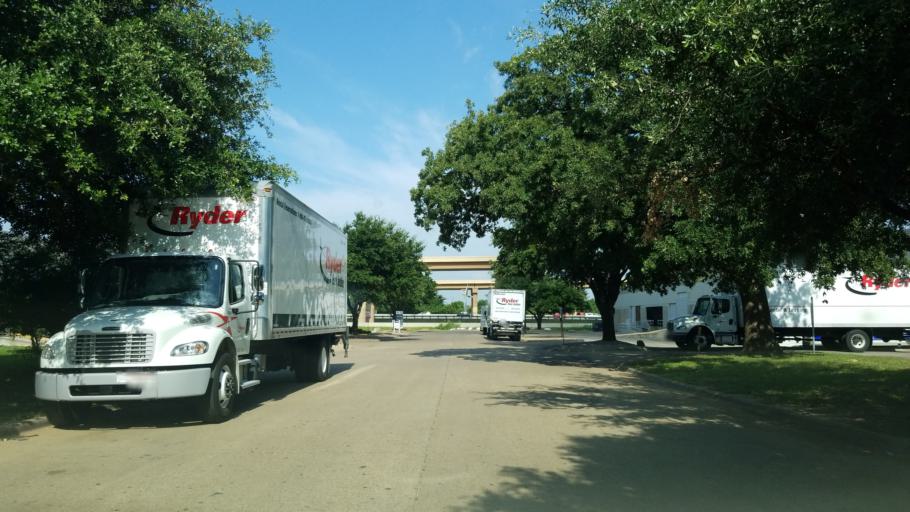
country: US
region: Texas
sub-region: Dallas County
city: Farmers Branch
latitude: 32.8839
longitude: -96.8960
